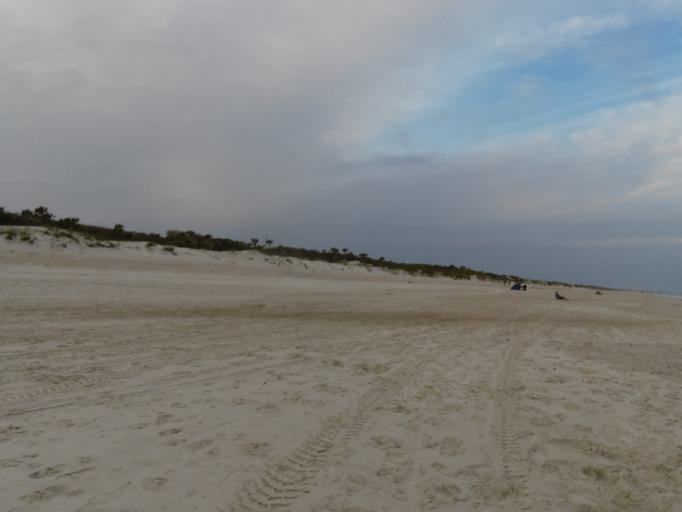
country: US
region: Florida
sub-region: Duval County
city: Atlantic Beach
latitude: 30.3615
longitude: -81.3973
